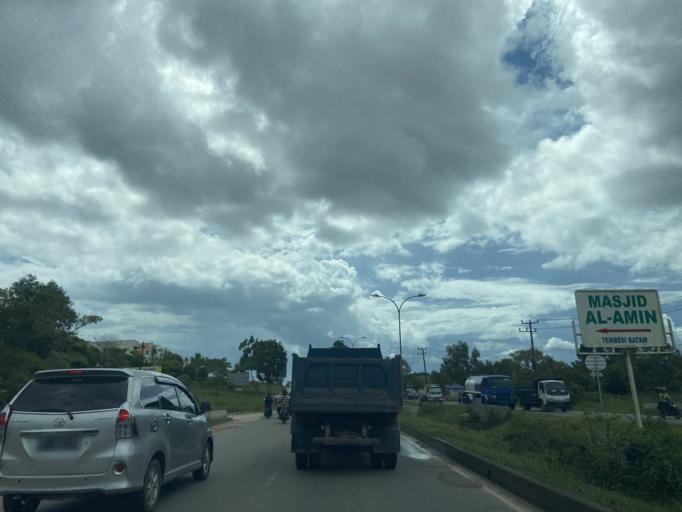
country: SG
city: Singapore
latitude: 1.0394
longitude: 103.9957
